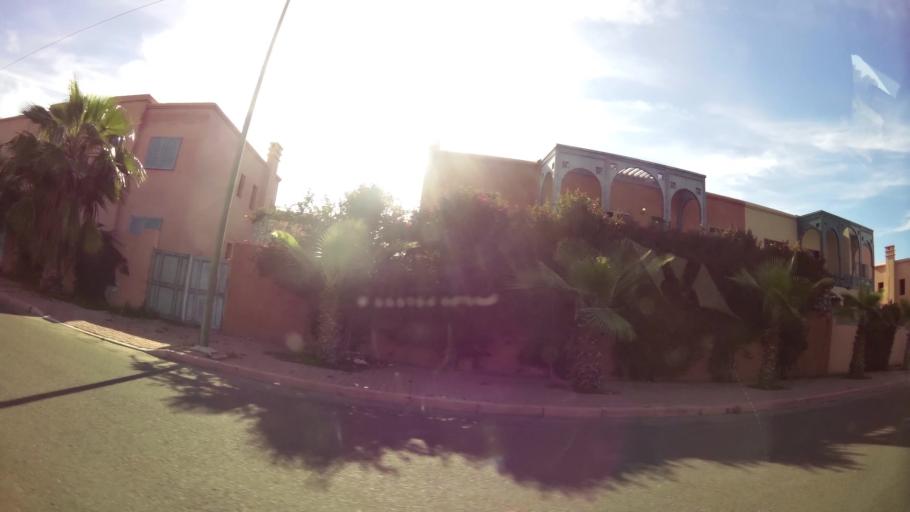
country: MA
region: Marrakech-Tensift-Al Haouz
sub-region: Marrakech
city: Marrakesh
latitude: 31.6757
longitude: -8.0518
